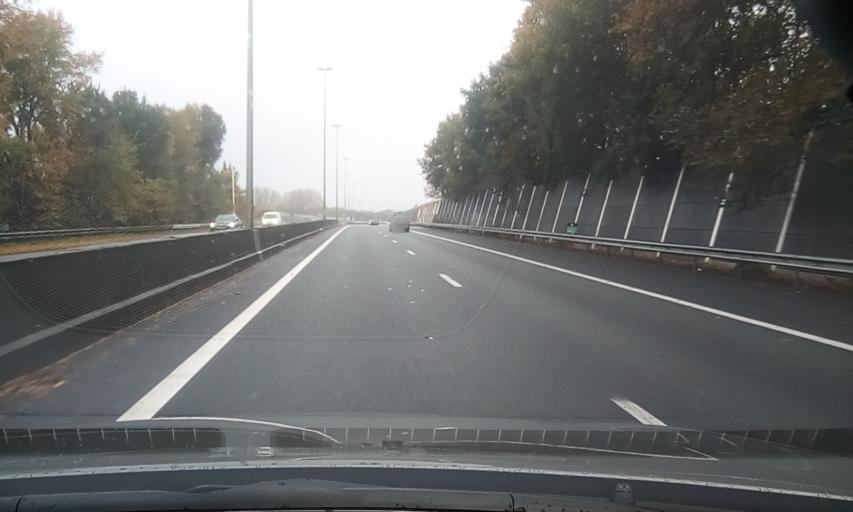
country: NL
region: Groningen
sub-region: Gemeente Groningen
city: Groningen
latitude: 53.1918
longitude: 6.5664
